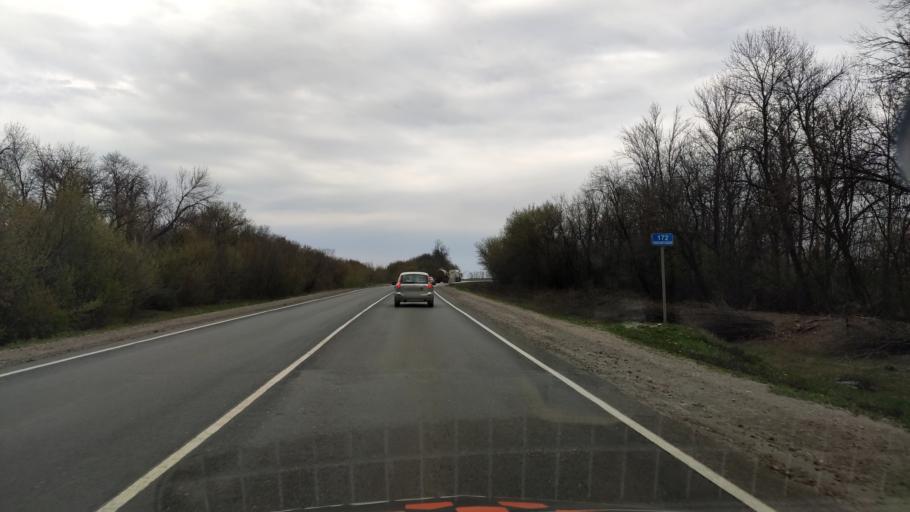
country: RU
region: Voronezj
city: Nizhnedevitsk
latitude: 51.5817
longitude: 38.4944
